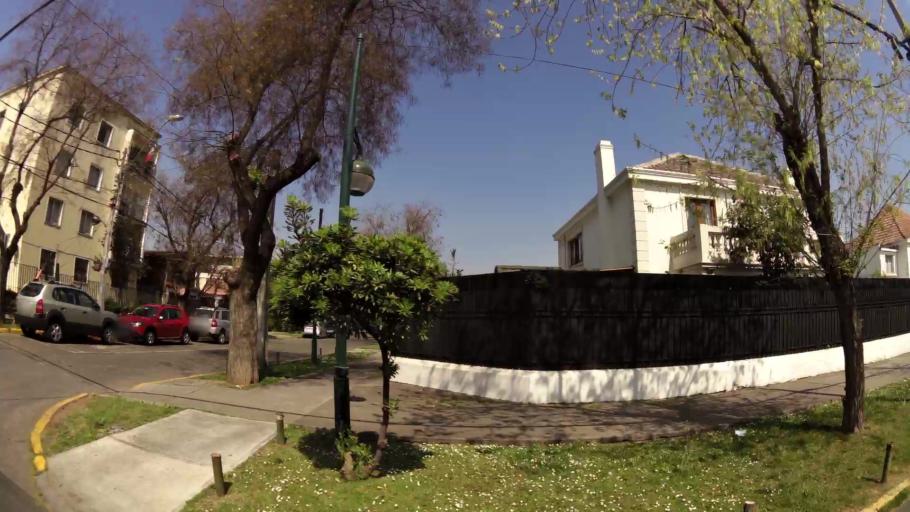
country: CL
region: Santiago Metropolitan
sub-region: Provincia de Santiago
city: Villa Presidente Frei, Nunoa, Santiago, Chile
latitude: -33.4605
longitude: -70.6069
